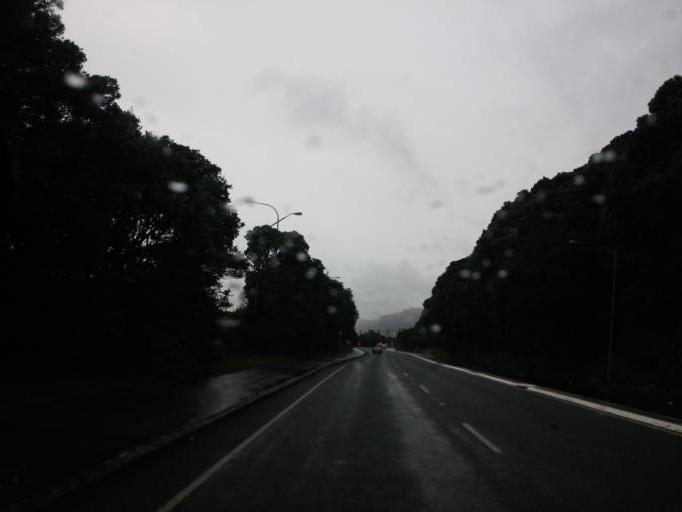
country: NZ
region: Wellington
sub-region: Wellington City
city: Wellington
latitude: -41.2505
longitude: 174.8084
